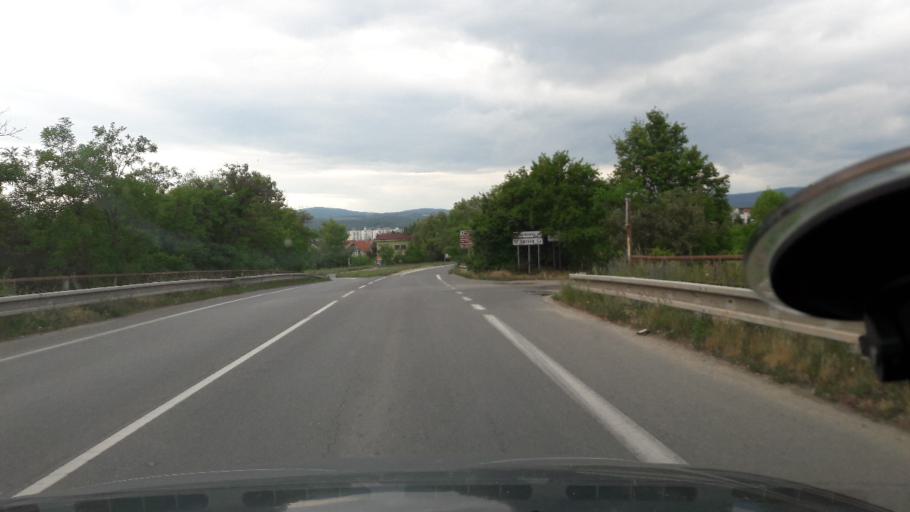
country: SK
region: Bratislavsky
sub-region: Okres Pezinok
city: Pezinok
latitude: 48.2878
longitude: 17.2810
